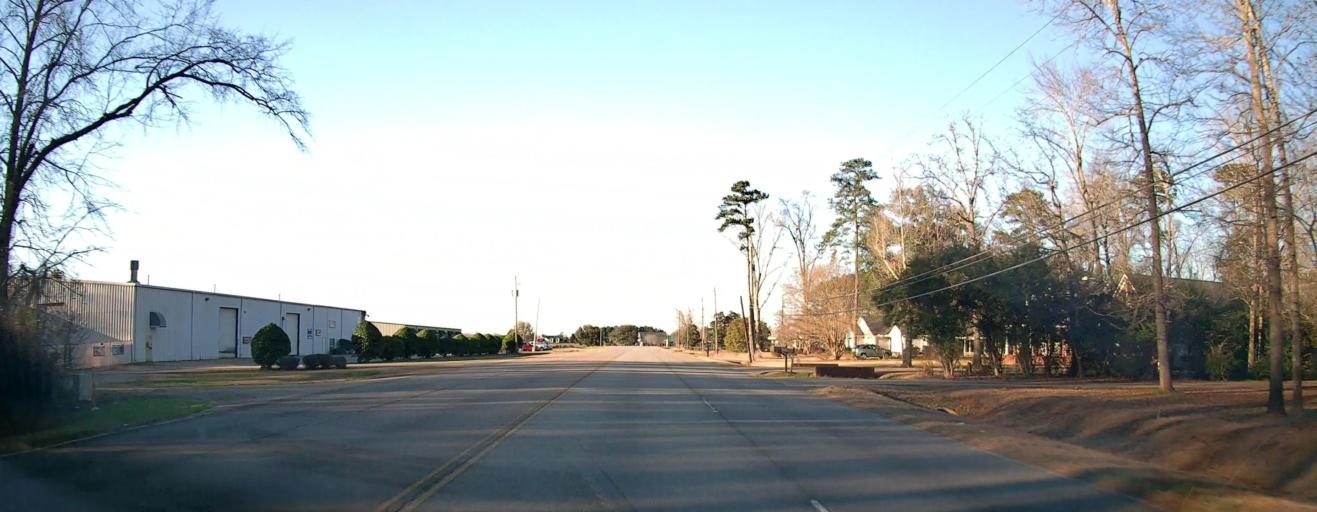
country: US
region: Georgia
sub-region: Dougherty County
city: Albany
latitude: 31.6270
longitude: -84.2295
